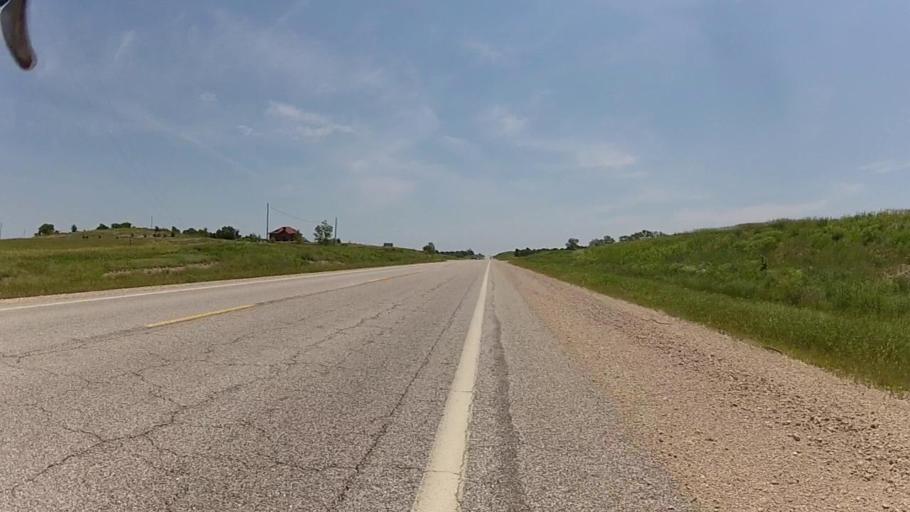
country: US
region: Kansas
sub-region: Chautauqua County
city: Sedan
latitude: 37.1132
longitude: -96.4547
